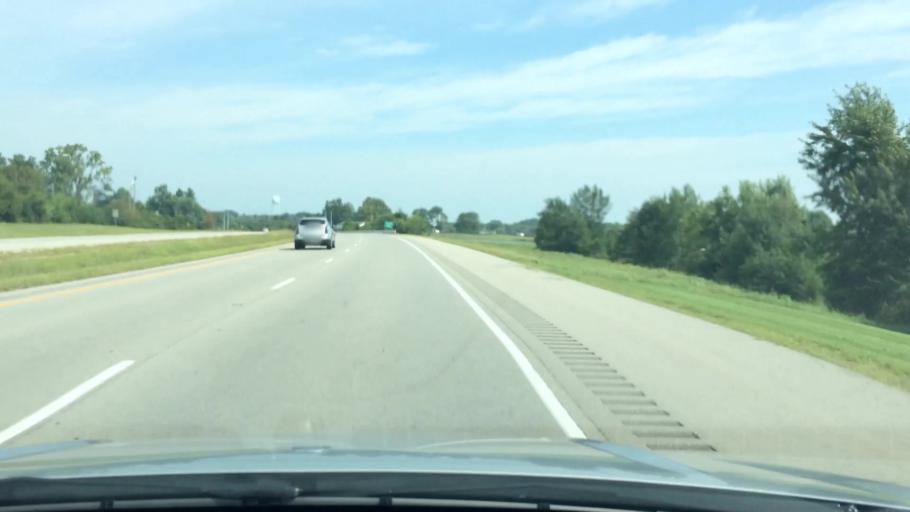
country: US
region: Kentucky
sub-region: Anderson County
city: Lawrenceburg
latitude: 38.1075
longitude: -84.9150
